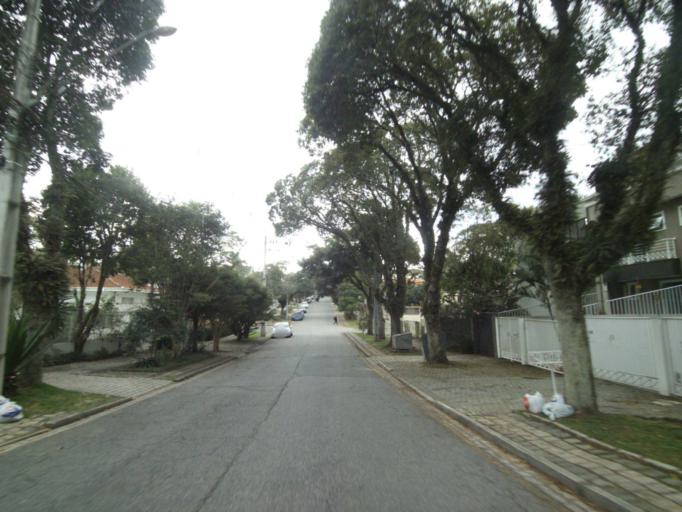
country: BR
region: Parana
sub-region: Curitiba
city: Curitiba
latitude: -25.4218
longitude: -49.2791
